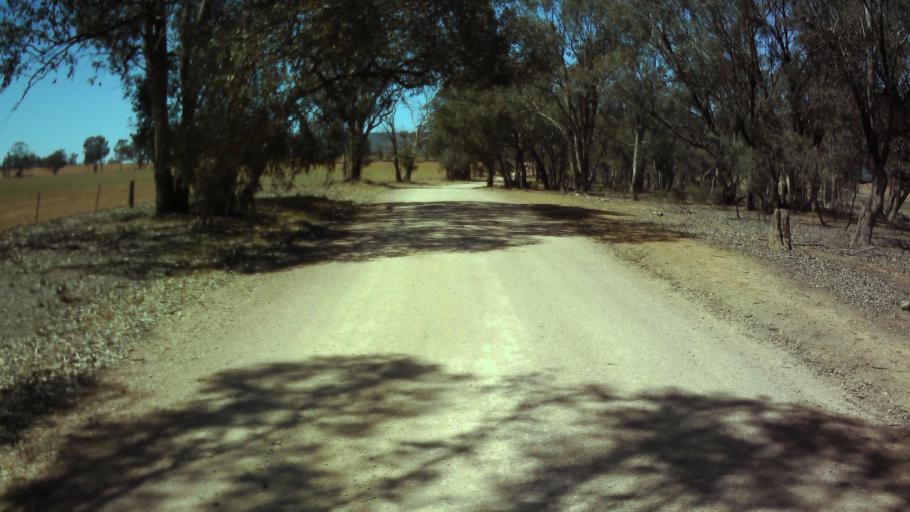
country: AU
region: New South Wales
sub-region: Weddin
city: Grenfell
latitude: -33.9280
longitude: 148.0781
